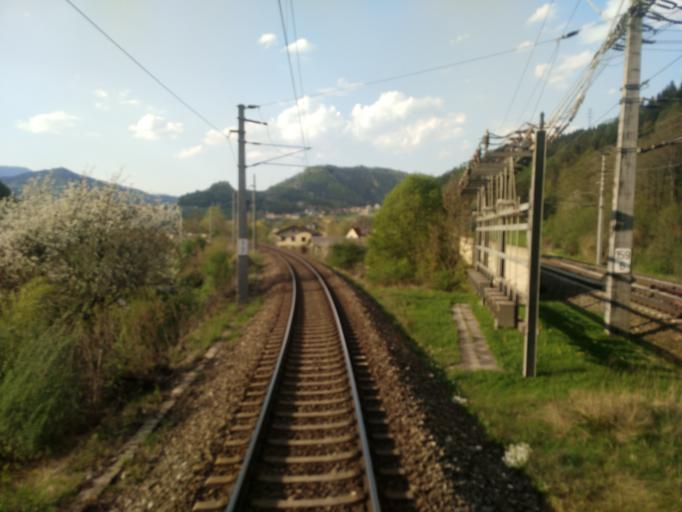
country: AT
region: Styria
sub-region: Politischer Bezirk Bruck-Muerzzuschlag
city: Bruck an der Mur
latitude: 47.4003
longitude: 15.2884
